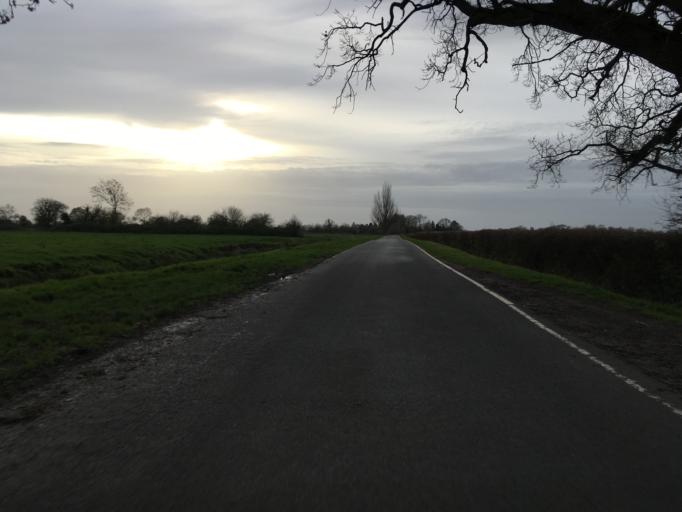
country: GB
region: Wales
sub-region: Newport
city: Redwick
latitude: 51.5584
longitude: -2.8341
